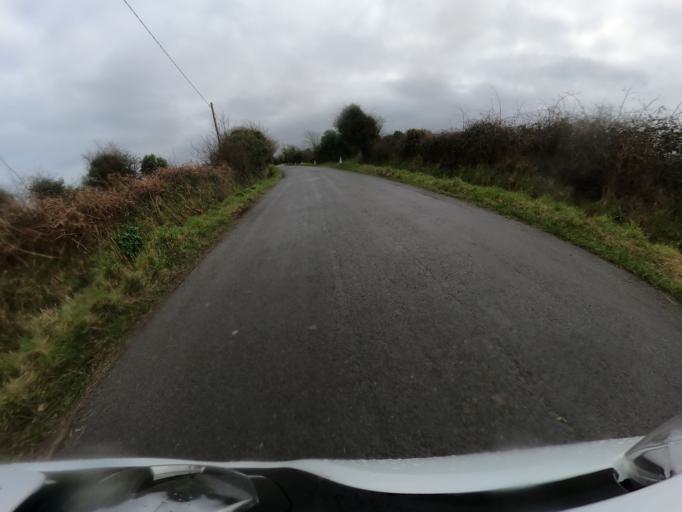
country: IM
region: Ramsey
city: Ramsey
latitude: 54.3789
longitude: -4.4476
